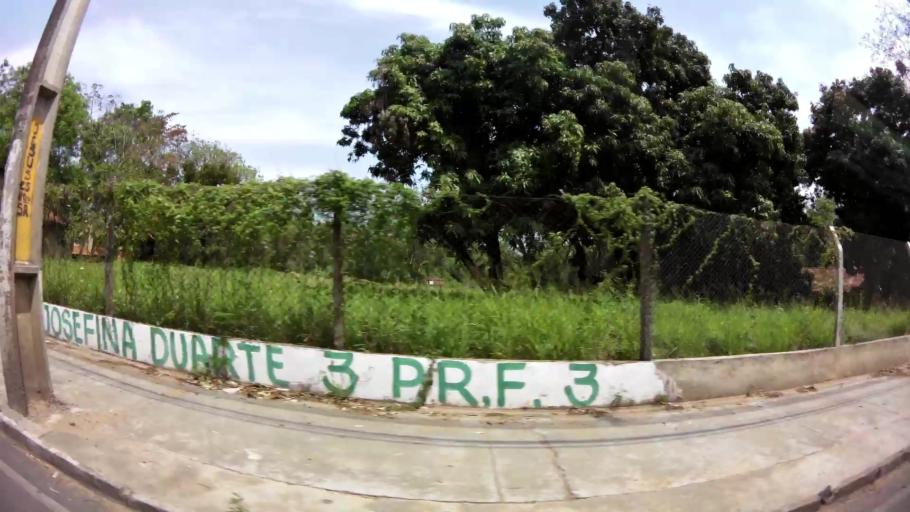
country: PY
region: Asuncion
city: Asuncion
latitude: -25.2807
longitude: -57.5870
